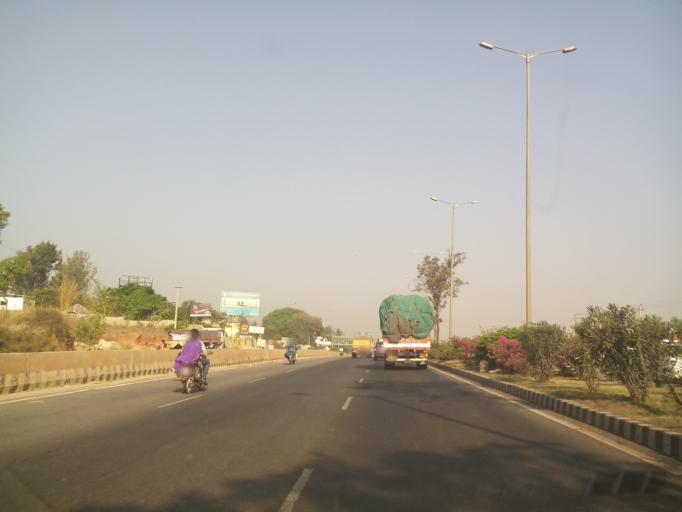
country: IN
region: Karnataka
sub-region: Bangalore Rural
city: Nelamangala
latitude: 13.0870
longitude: 77.4083
